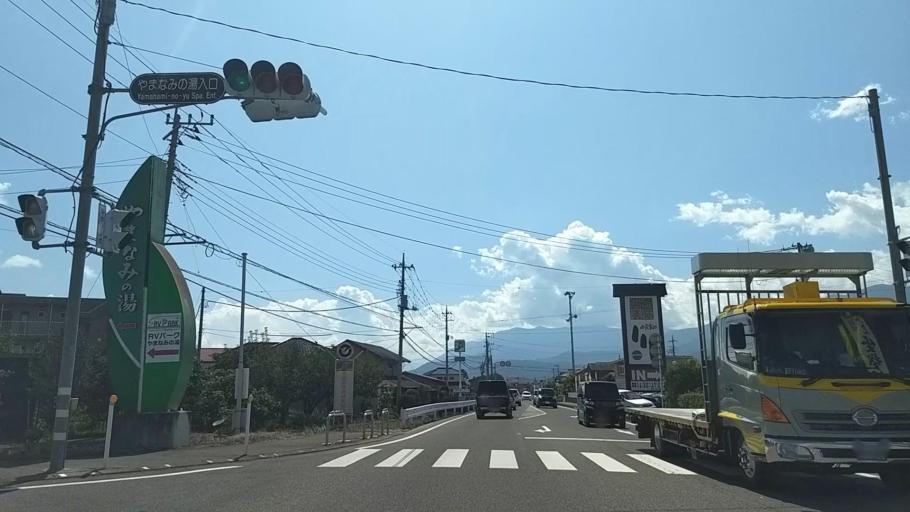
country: JP
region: Yamanashi
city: Ryuo
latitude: 35.5859
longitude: 138.4967
